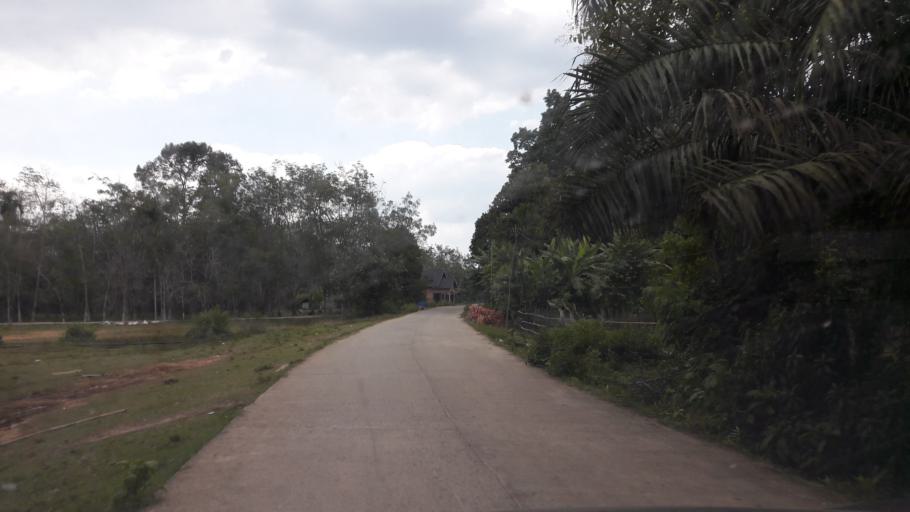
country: ID
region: South Sumatra
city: Prabumulih
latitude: -3.3342
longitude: 104.1098
